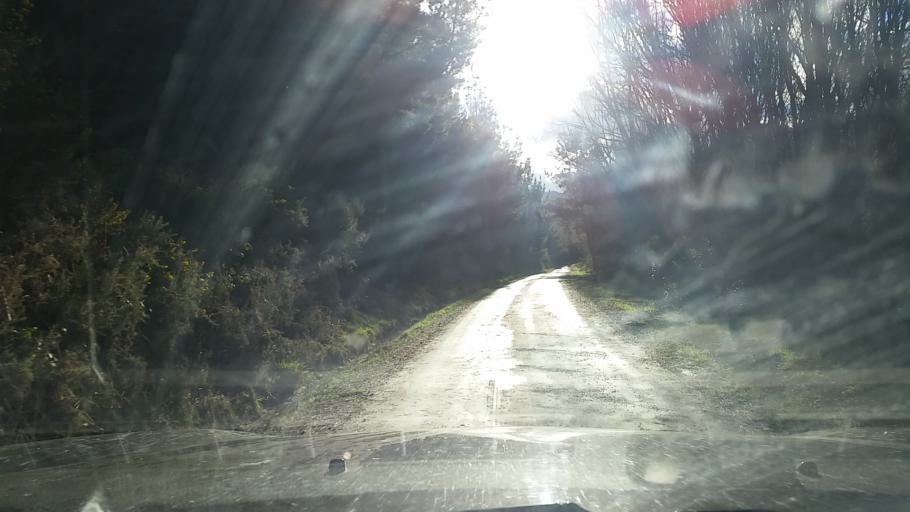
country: NZ
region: Nelson
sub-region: Nelson City
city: Nelson
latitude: -41.5548
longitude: 173.4260
